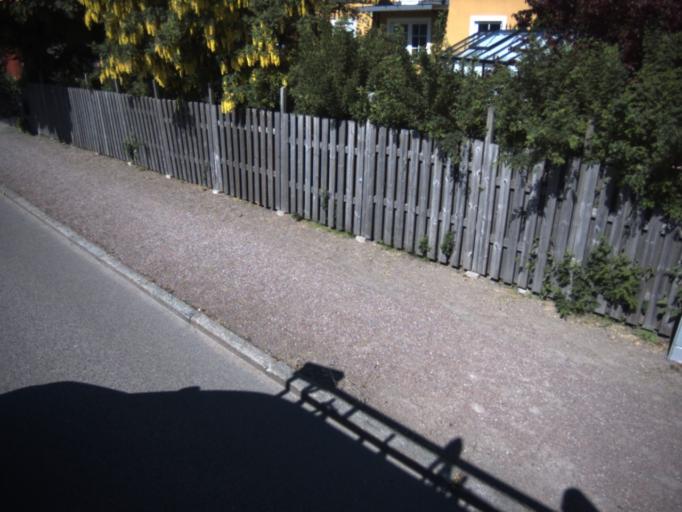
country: SE
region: Skane
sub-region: Helsingborg
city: Helsingborg
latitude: 56.0186
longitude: 12.7140
